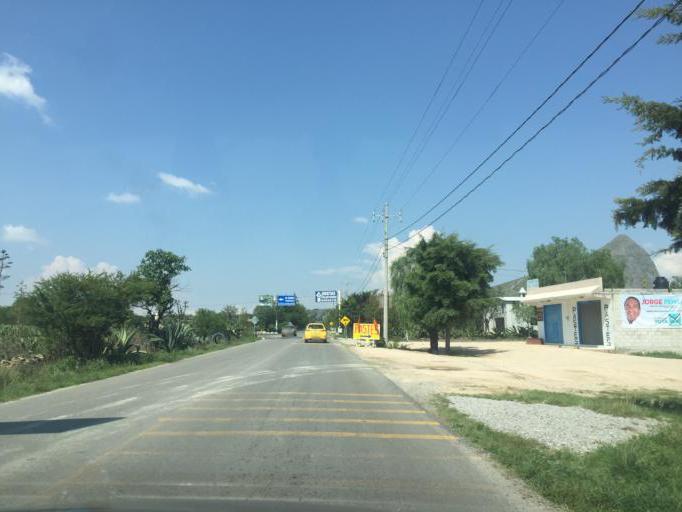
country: MX
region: Hidalgo
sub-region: Cardonal
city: Pozuelos
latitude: 20.6115
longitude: -99.0860
